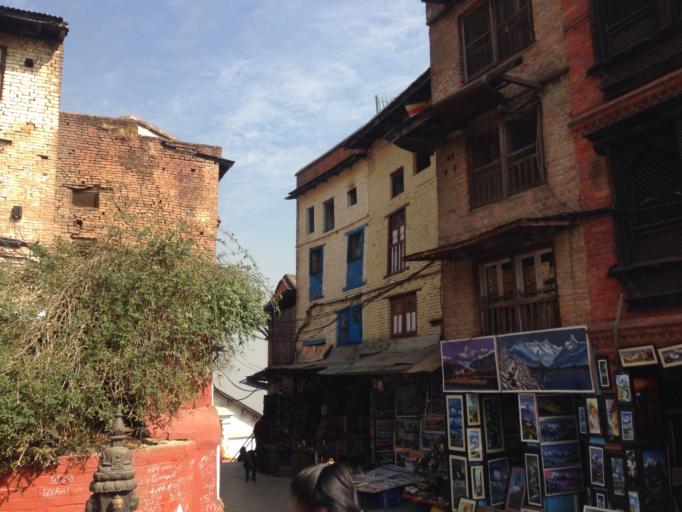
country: NP
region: Central Region
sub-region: Bagmati Zone
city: Kathmandu
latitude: 27.7152
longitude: 85.2901
